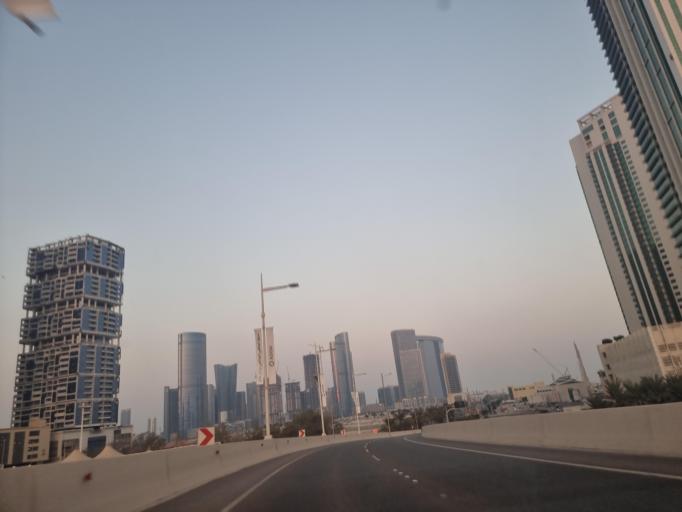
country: AE
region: Abu Dhabi
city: Abu Dhabi
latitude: 24.4936
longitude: 54.3912
